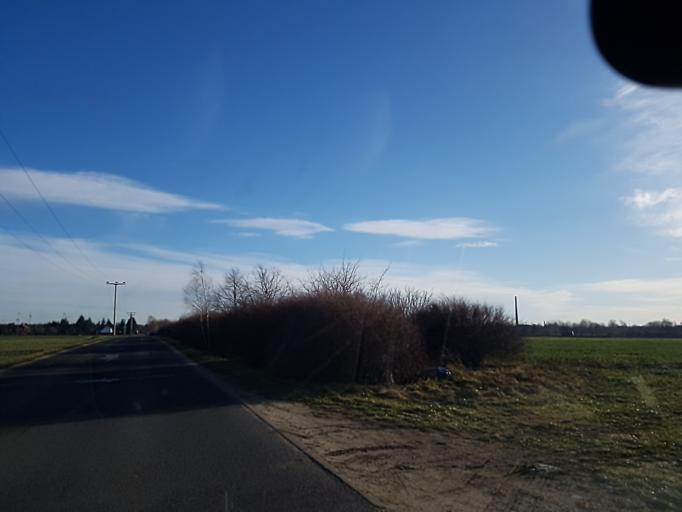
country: DE
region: Brandenburg
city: Finsterwalde
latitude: 51.6483
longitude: 13.7162
